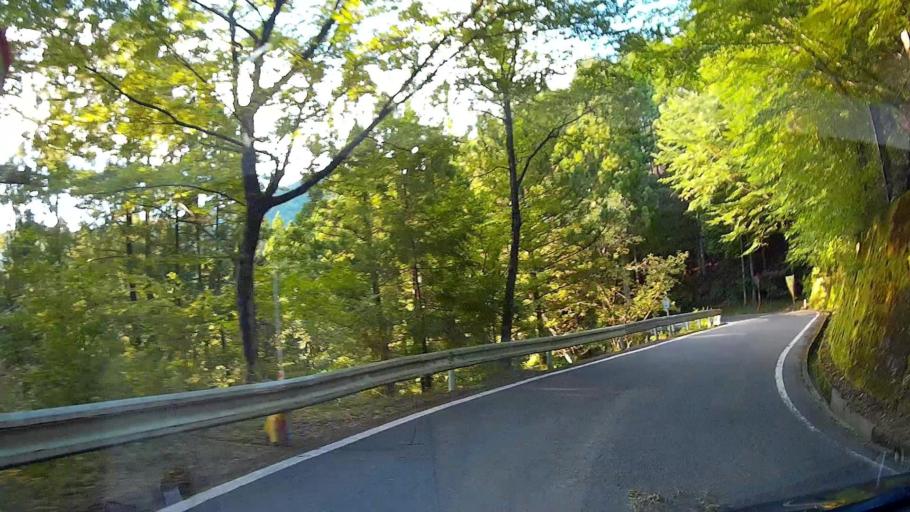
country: JP
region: Shizuoka
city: Shizuoka-shi
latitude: 35.1584
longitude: 138.2611
